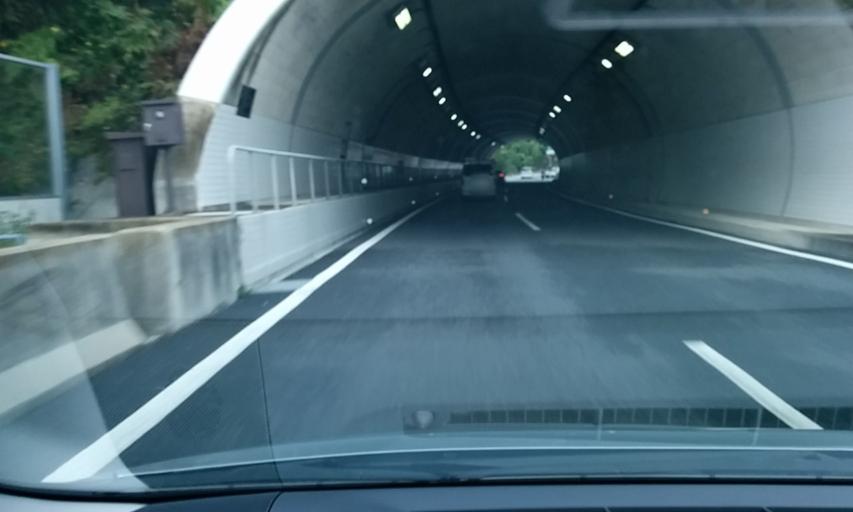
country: JP
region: Kyoto
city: Muko
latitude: 34.9226
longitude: 135.6693
